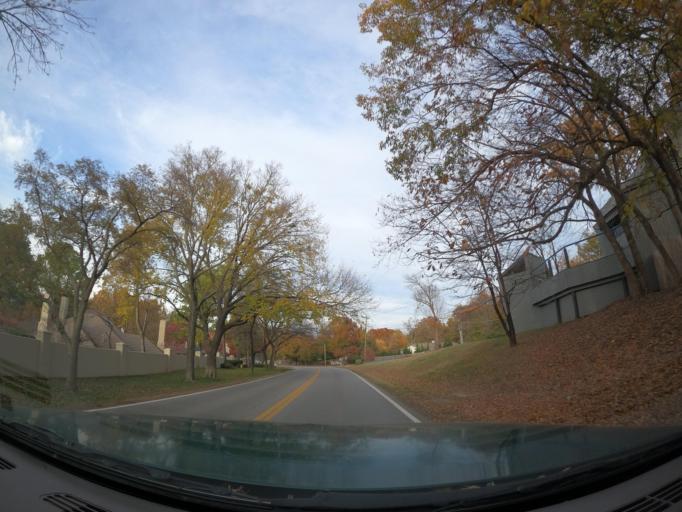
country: US
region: Oklahoma
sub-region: Tulsa County
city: Jenks
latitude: 36.0542
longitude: -95.9404
